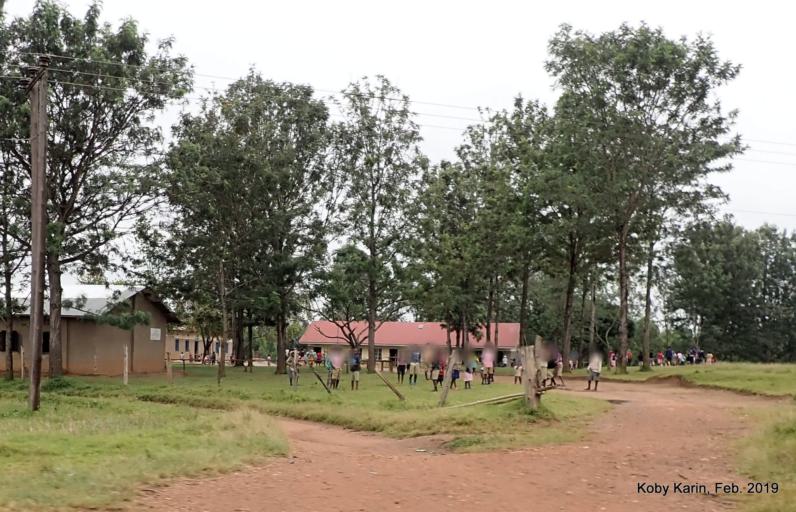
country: UG
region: Western Region
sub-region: Bushenyi District
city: Bushenyi
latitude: -0.5142
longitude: 30.1159
